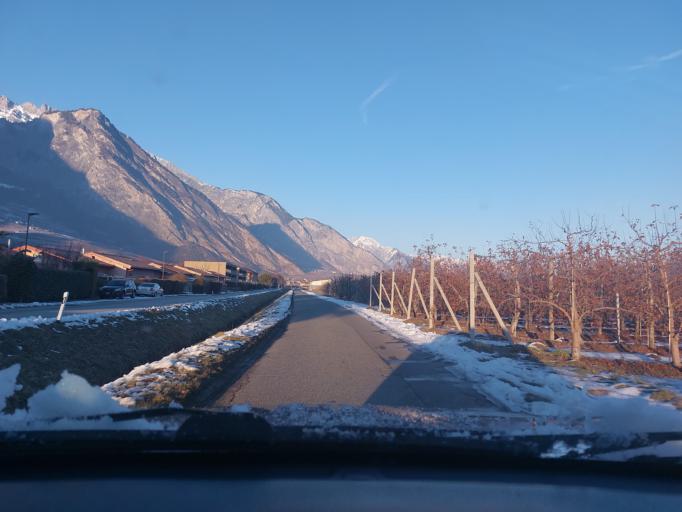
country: CH
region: Valais
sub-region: Martigny District
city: Saillon
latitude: 46.1682
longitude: 7.1929
